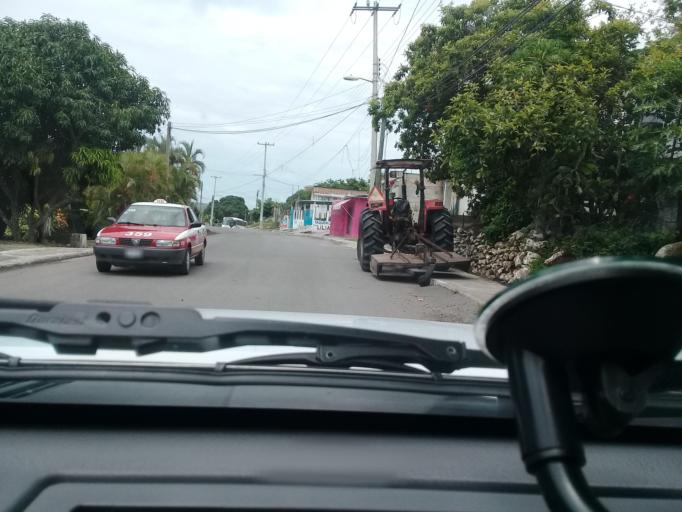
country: MX
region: Veracruz
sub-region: Paso de Ovejas
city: El Hatito
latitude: 19.2786
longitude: -96.3916
